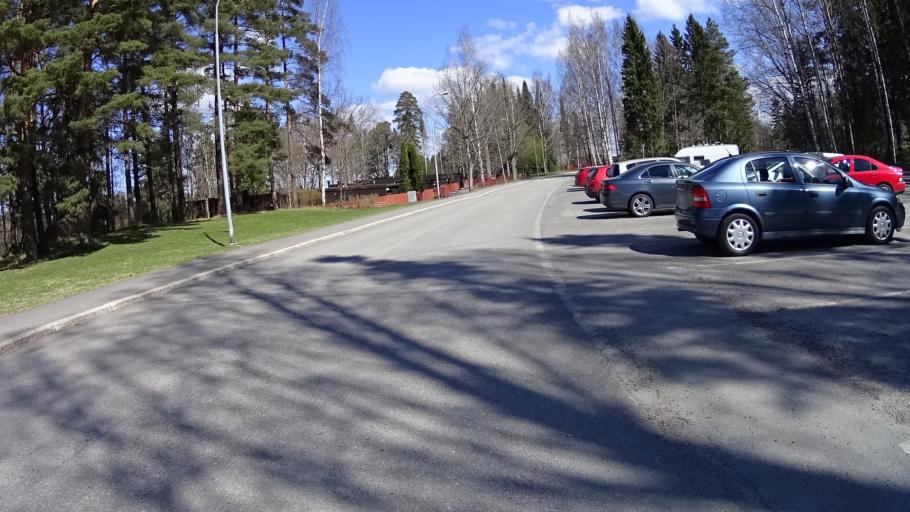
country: FI
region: Uusimaa
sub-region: Helsinki
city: Kauniainen
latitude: 60.2433
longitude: 24.7355
